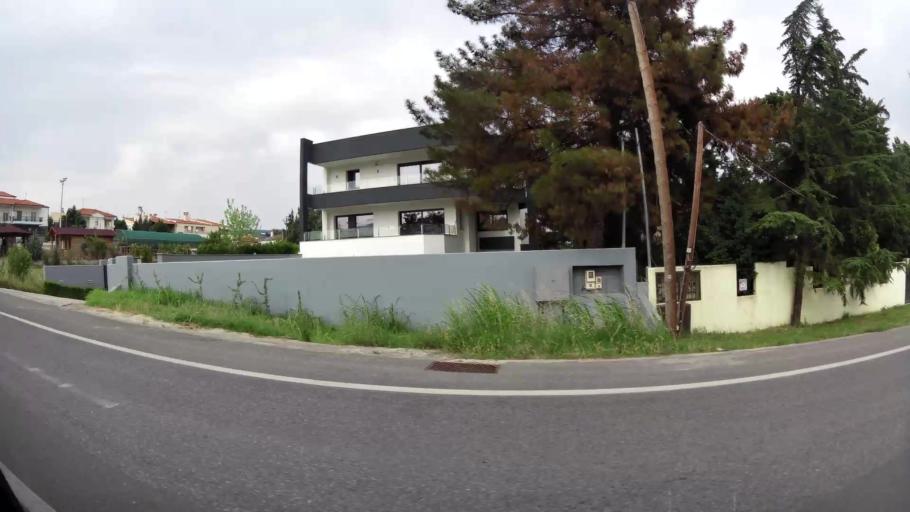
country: GR
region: Central Macedonia
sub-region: Nomos Thessalonikis
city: Oraiokastro
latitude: 40.7213
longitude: 22.9253
